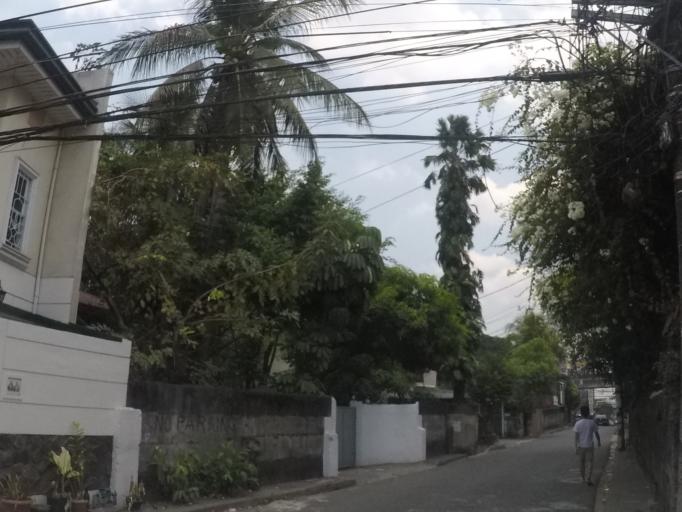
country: PH
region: Metro Manila
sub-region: San Juan
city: San Juan
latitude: 14.6093
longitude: 121.0260
